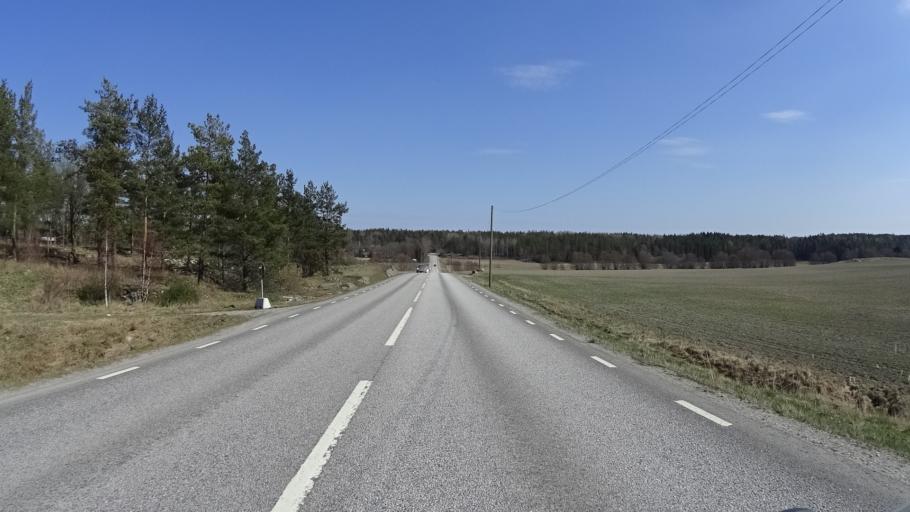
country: SE
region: Stockholm
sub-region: Osterakers Kommun
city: Akersberga
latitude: 59.4507
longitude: 18.2198
